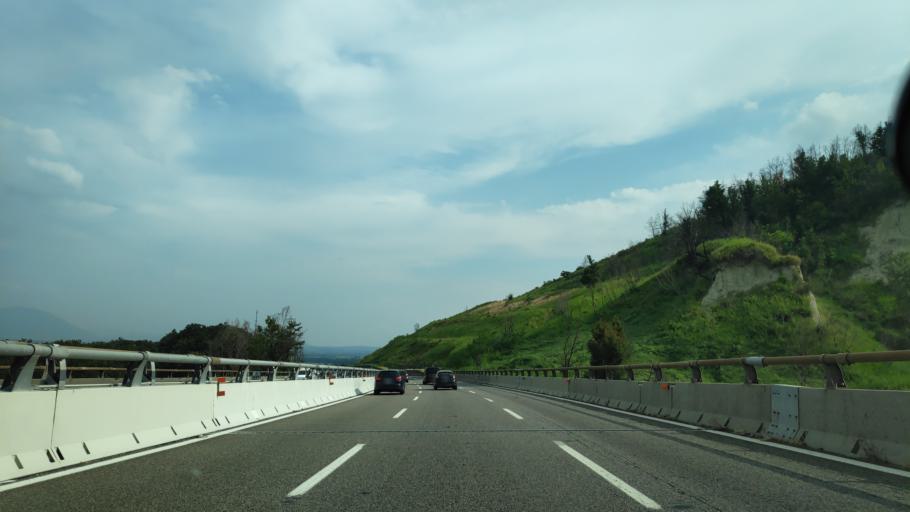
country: IT
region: Latium
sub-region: Citta metropolitana di Roma Capitale
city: Nazzano
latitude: 42.2110
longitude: 12.6013
